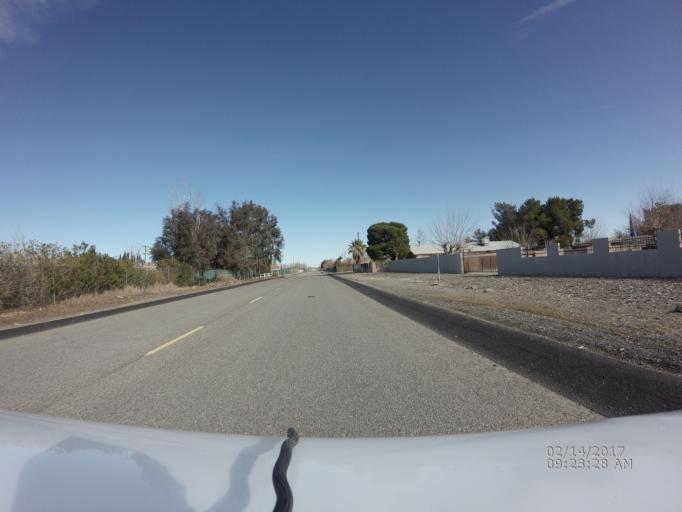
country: US
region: California
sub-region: Los Angeles County
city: Littlerock
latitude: 34.5664
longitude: -117.9476
